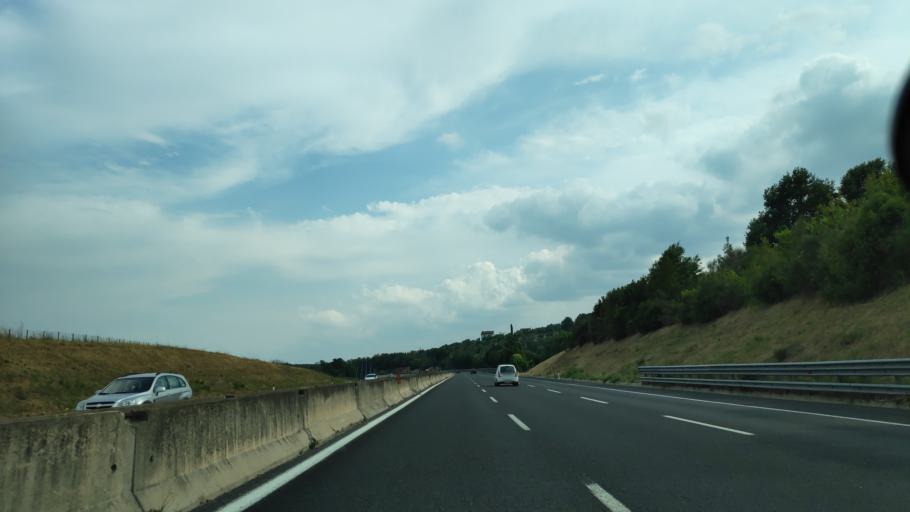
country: IT
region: Latium
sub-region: Citta metropolitana di Roma Capitale
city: Fiano Romano
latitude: 42.1846
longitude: 12.6025
